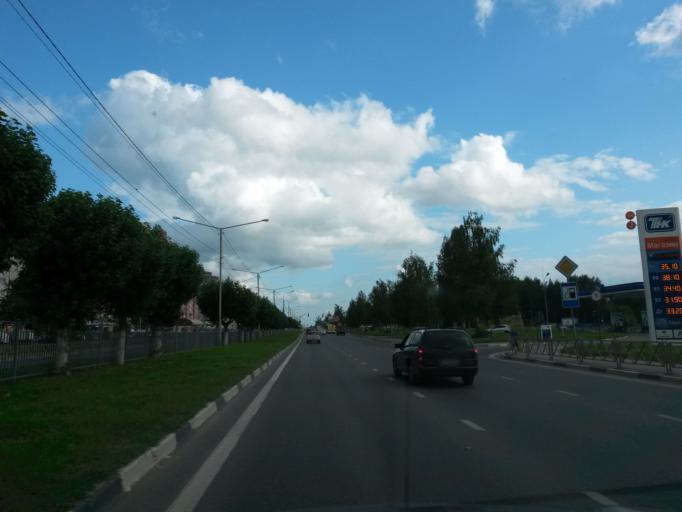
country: RU
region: Jaroslavl
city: Yaroslavl
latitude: 57.5854
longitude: 39.9061
